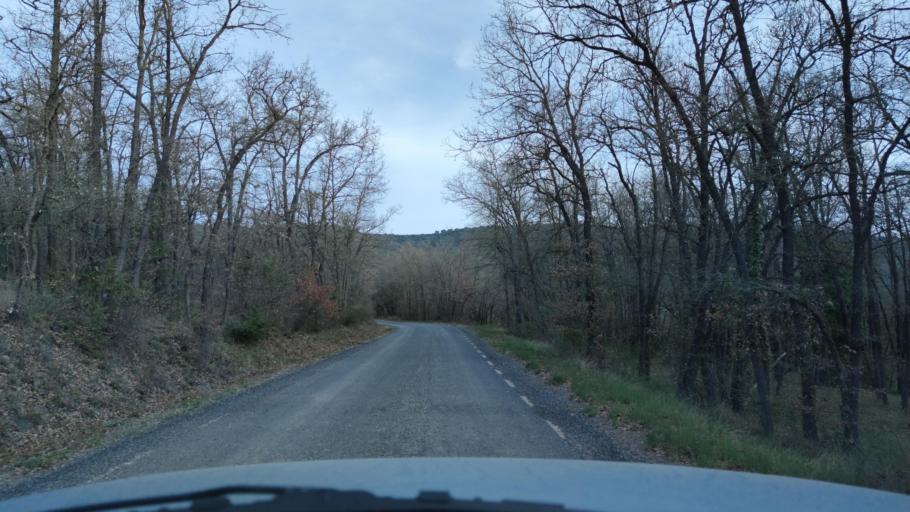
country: ES
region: Catalonia
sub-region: Provincia de Lleida
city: Camarasa
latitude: 41.8934
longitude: 0.8015
